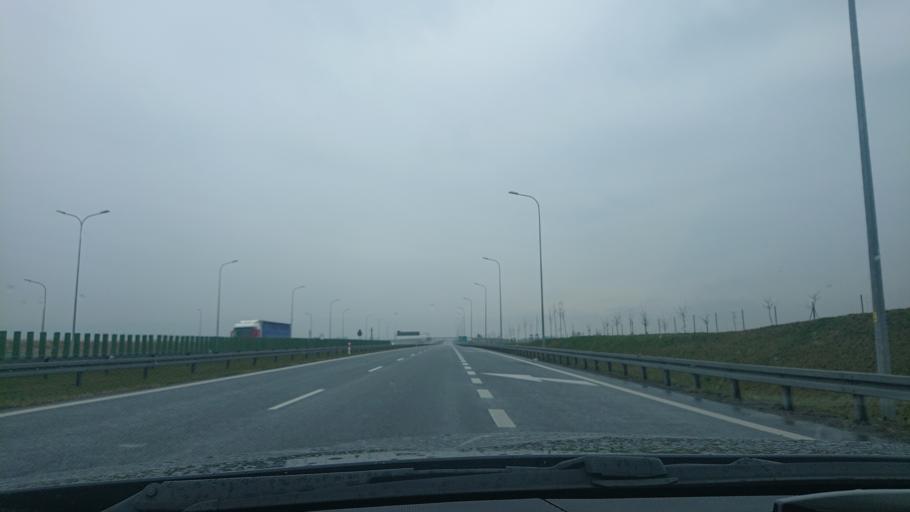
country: PL
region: Greater Poland Voivodeship
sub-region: Powiat gnieznienski
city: Gniezno
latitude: 52.5544
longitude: 17.5411
